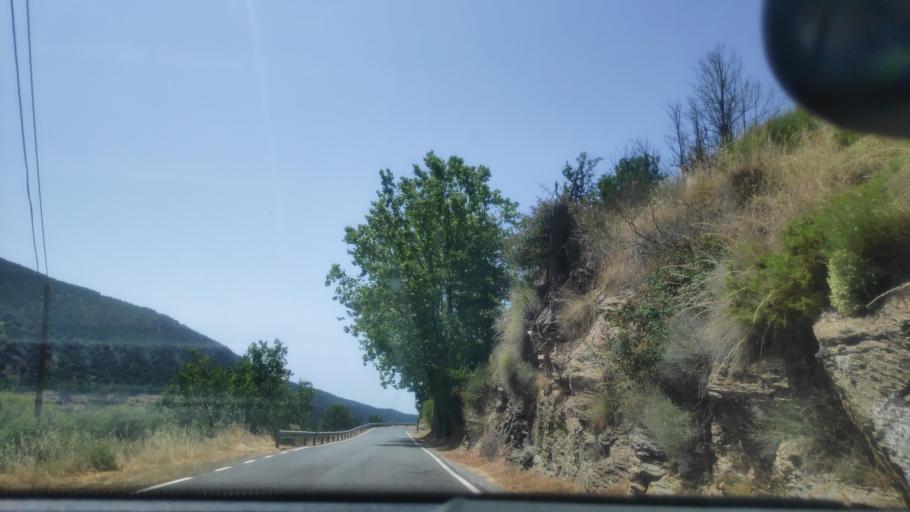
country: ES
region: Andalusia
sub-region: Provincia de Granada
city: Trevelez
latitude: 36.9884
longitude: -3.2718
